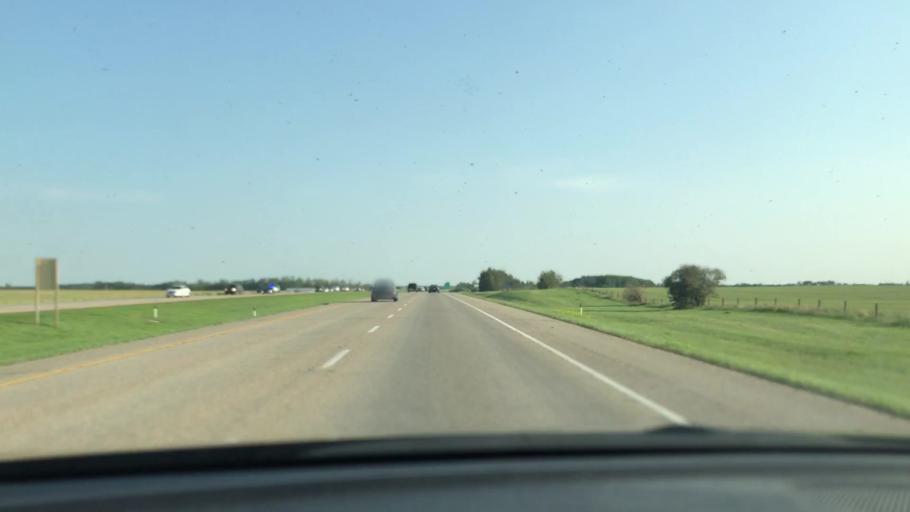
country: CA
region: Alberta
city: Millet
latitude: 53.1072
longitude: -113.5984
